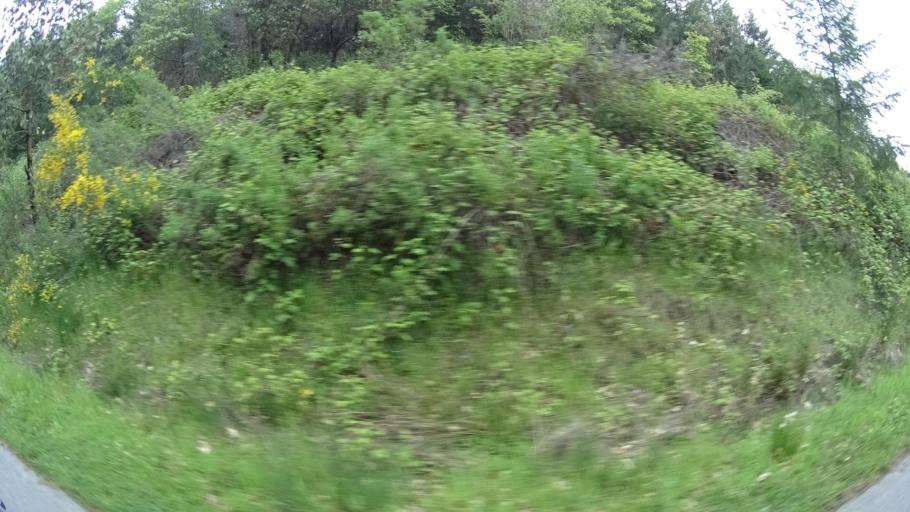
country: US
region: California
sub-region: Humboldt County
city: Willow Creek
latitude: 41.1213
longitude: -123.7423
